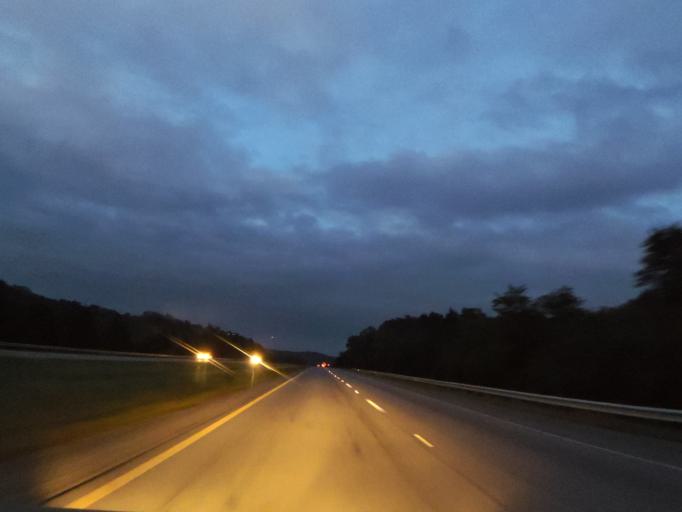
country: US
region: Alabama
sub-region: Jackson County
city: Scottsboro
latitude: 34.6199
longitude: -86.2068
